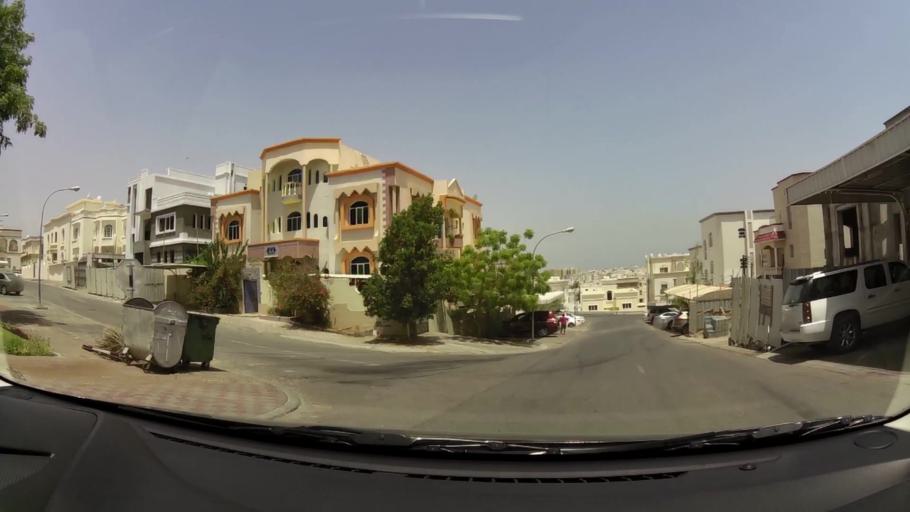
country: OM
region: Muhafazat Masqat
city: Bawshar
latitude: 23.5853
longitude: 58.4407
